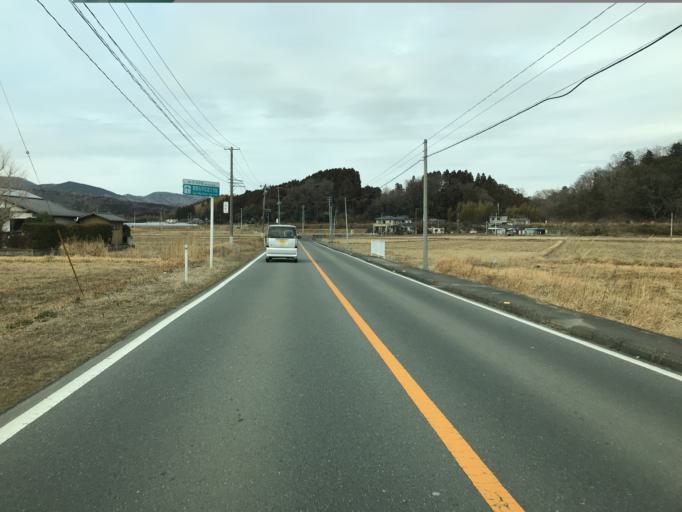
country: JP
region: Fukushima
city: Iwaki
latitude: 37.0900
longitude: 140.8741
